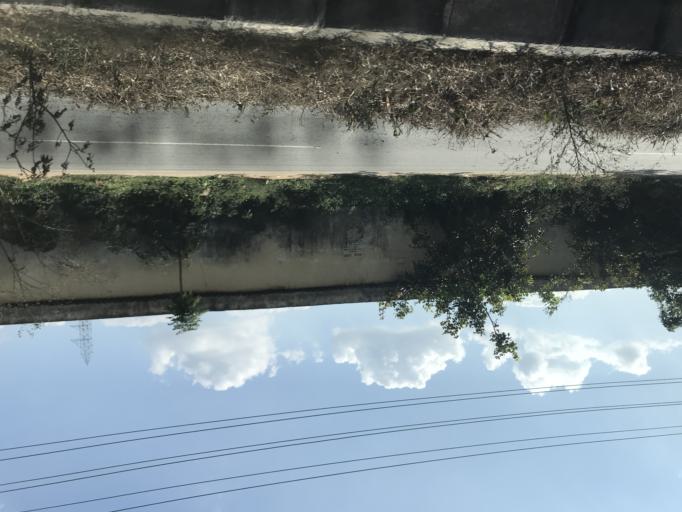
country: IN
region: Karnataka
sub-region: Bangalore Urban
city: Bangalore
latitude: 12.8261
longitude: 77.5864
